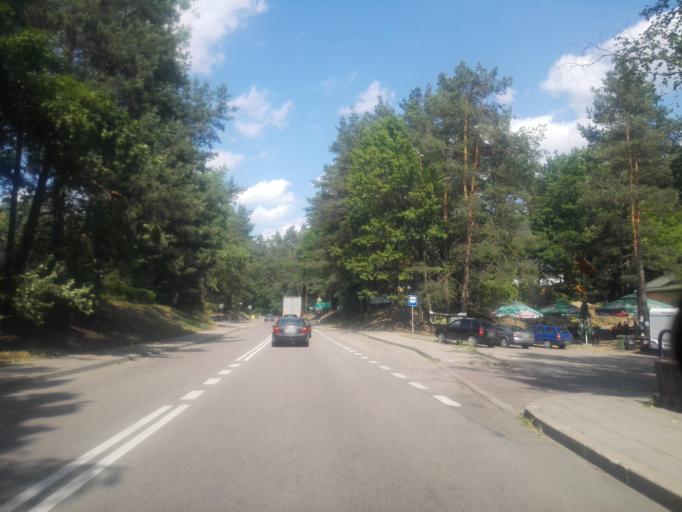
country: PL
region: Podlasie
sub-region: Powiat augustowski
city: Augustow
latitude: 53.8677
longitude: 23.0925
